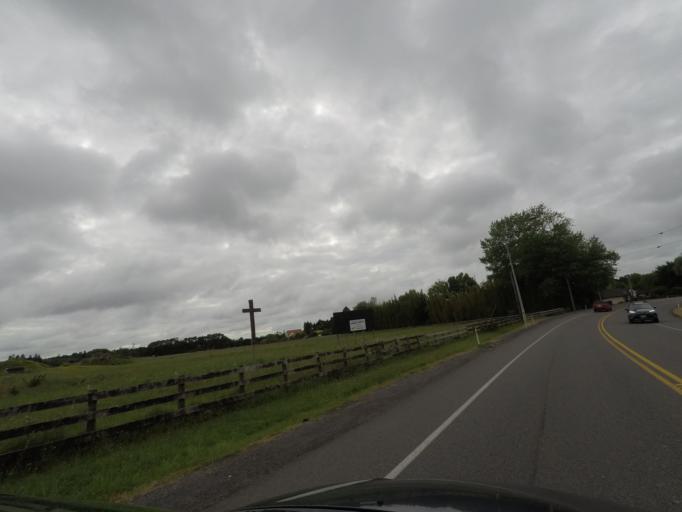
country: NZ
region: Auckland
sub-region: Auckland
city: Muriwai Beach
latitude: -36.7802
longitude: 174.5687
